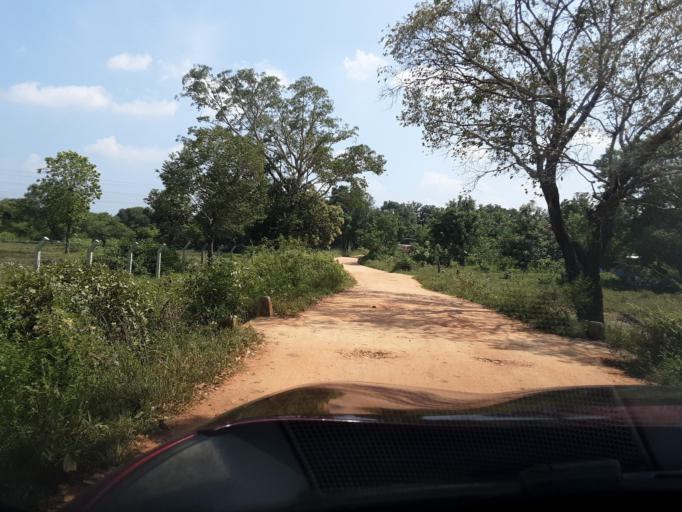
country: LK
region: Central
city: Sigiriya
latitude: 8.0059
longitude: 80.7457
